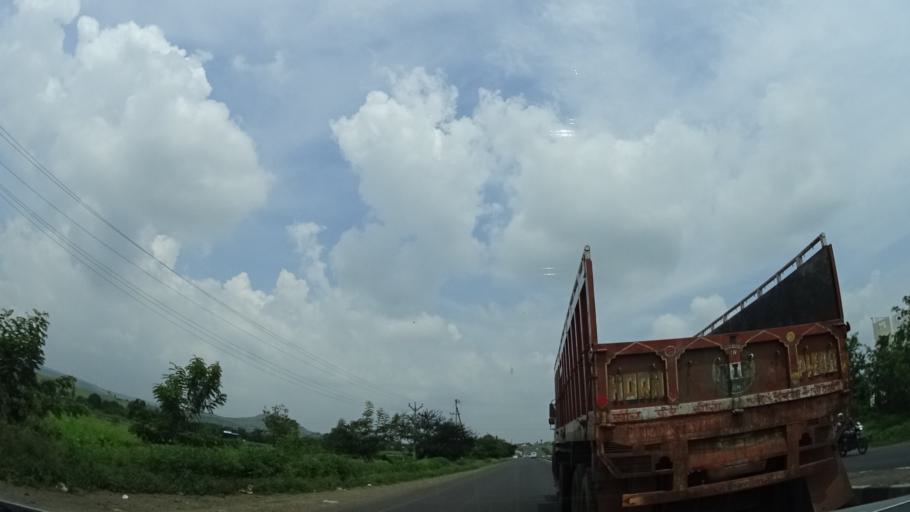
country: IN
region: Maharashtra
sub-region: Pune Division
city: Sirur
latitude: 18.9641
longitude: 74.5450
